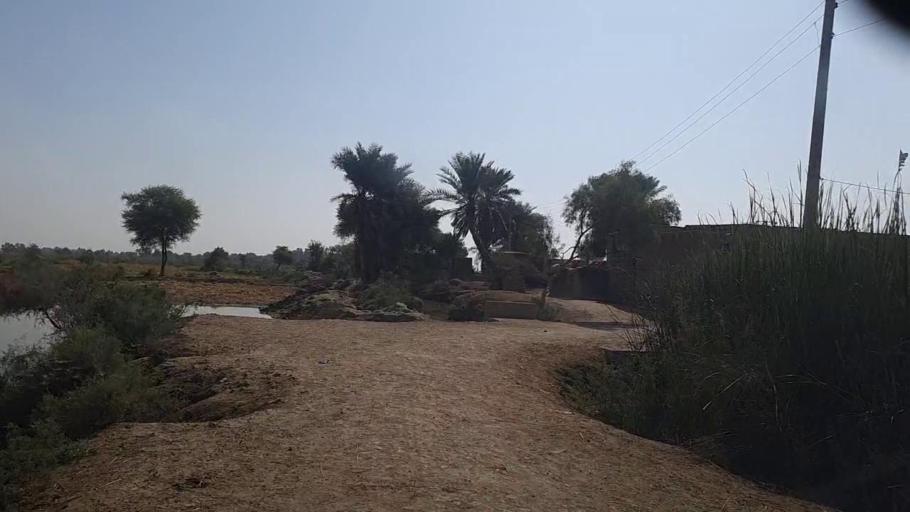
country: PK
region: Sindh
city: Thul
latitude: 28.1726
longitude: 68.7695
